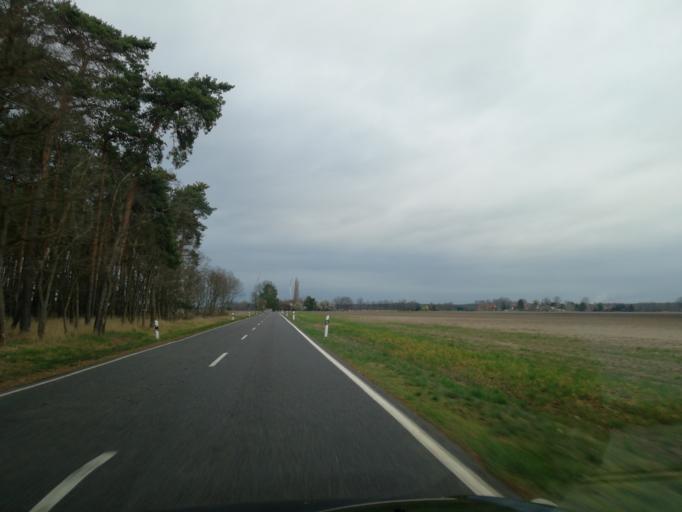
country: DE
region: Brandenburg
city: Vetschau
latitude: 51.7328
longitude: 14.1044
